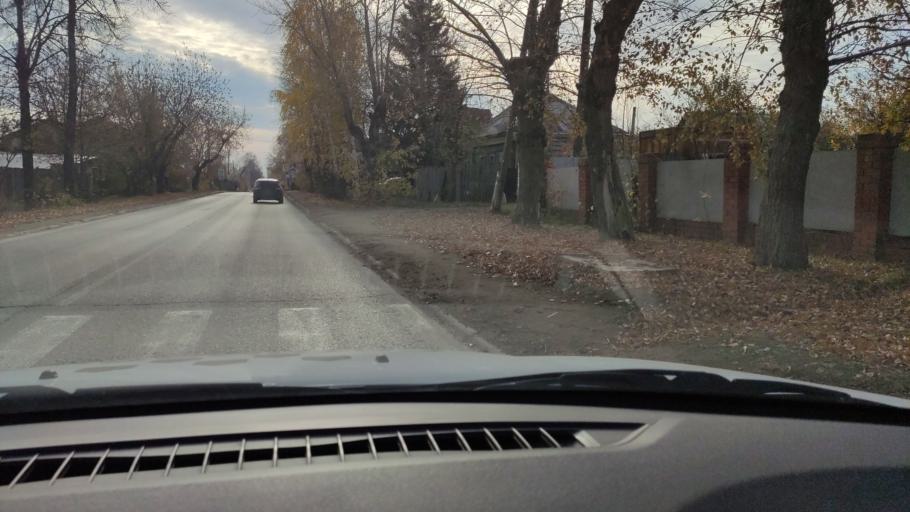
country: RU
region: Perm
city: Perm
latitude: 58.0176
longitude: 56.3139
